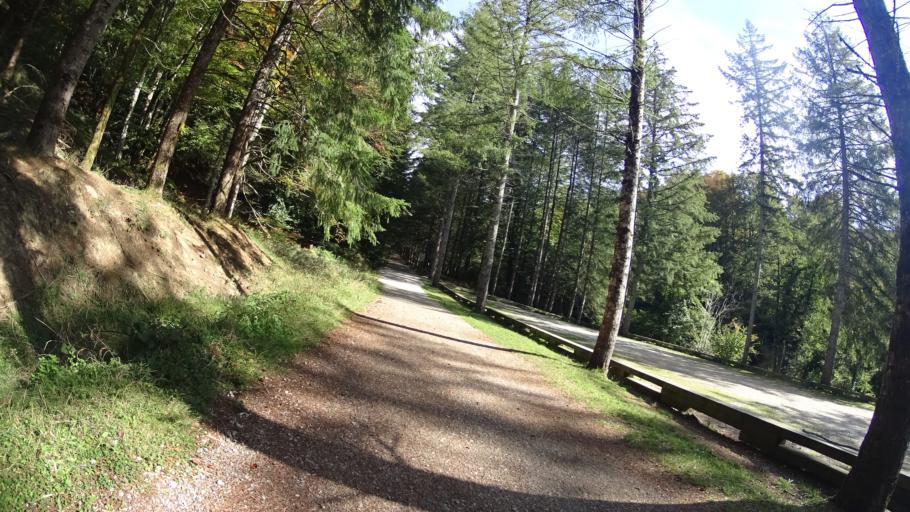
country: ES
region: Navarre
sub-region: Provincia de Navarra
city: Oronz
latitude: 42.9894
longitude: -1.1064
